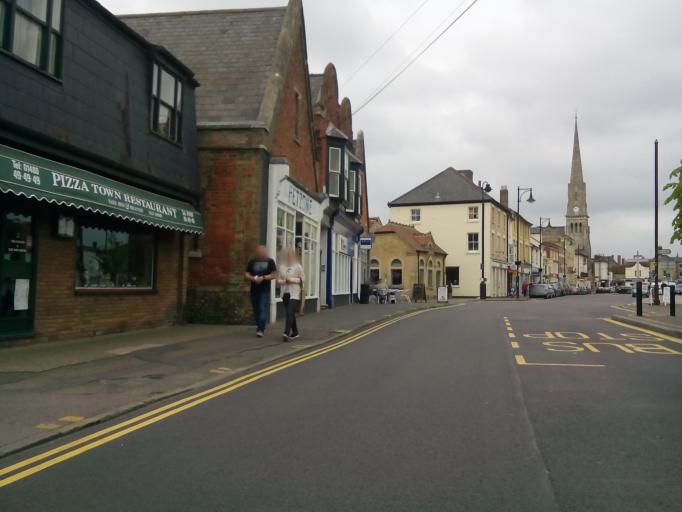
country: GB
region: England
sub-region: Cambridgeshire
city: Hemingford Grey
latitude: 52.3226
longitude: -0.0710
